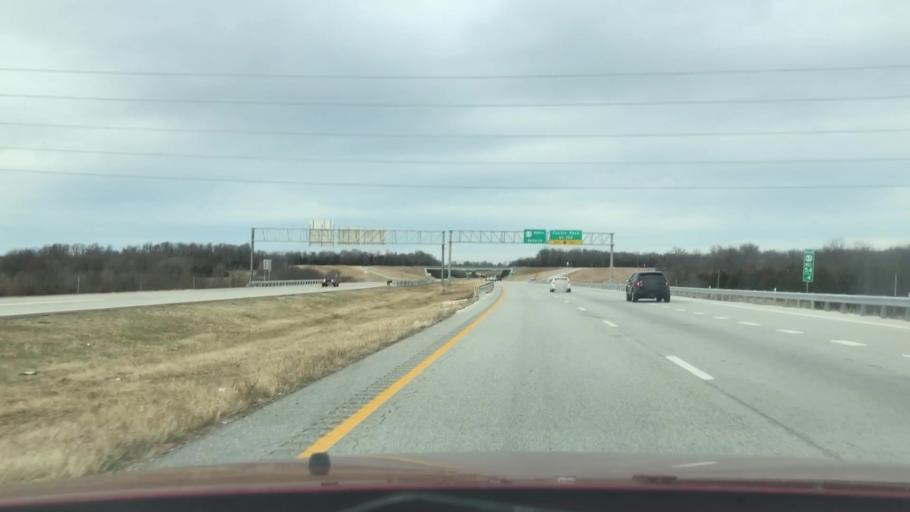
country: US
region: Missouri
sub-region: Greene County
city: Springfield
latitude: 37.2546
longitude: -93.2243
